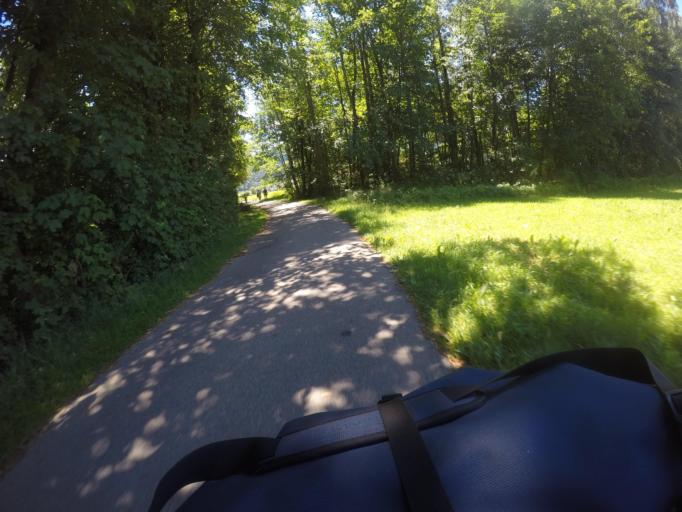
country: DE
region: Bavaria
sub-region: Swabia
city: Fuessen
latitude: 47.5769
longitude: 10.7124
